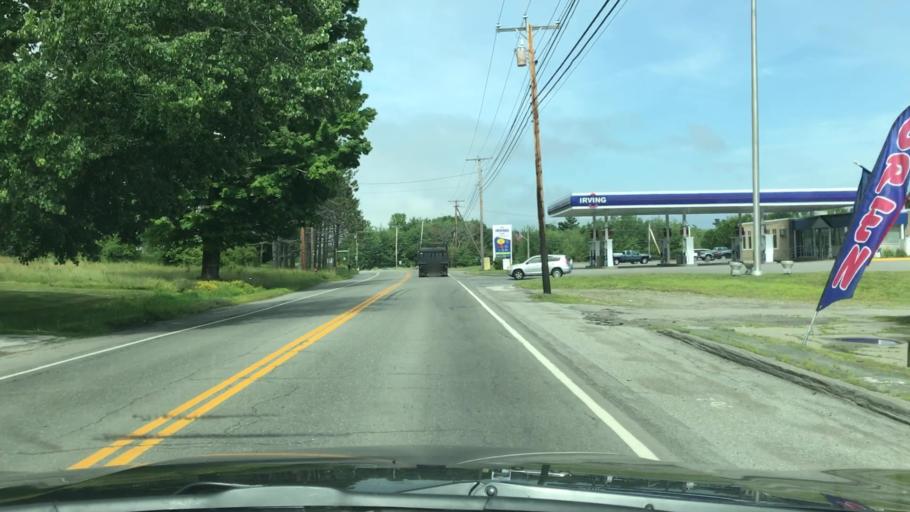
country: US
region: Maine
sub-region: Waldo County
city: Stockton Springs
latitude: 44.4632
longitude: -68.9053
